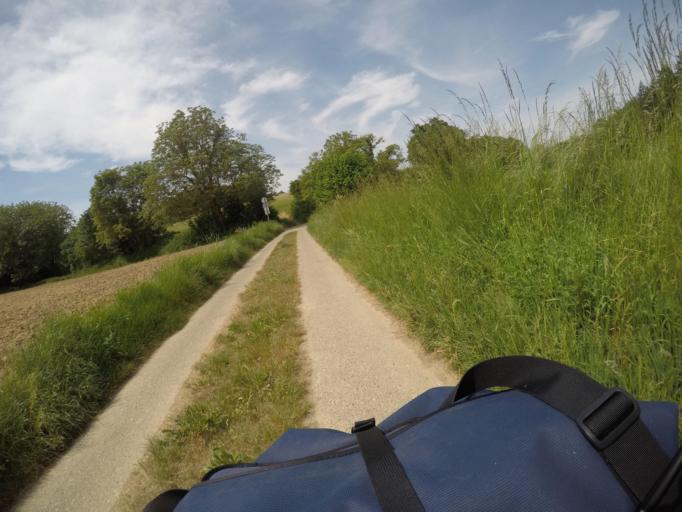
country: DE
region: Baden-Wuerttemberg
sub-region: Karlsruhe Region
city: Weingarten
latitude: 48.9778
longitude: 8.4964
